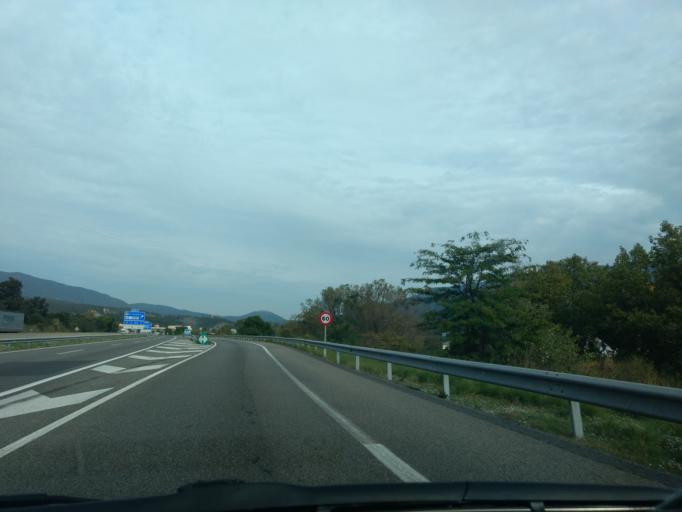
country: ES
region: Catalonia
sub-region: Provincia de Girona
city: la Jonquera
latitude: 42.3990
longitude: 2.8772
